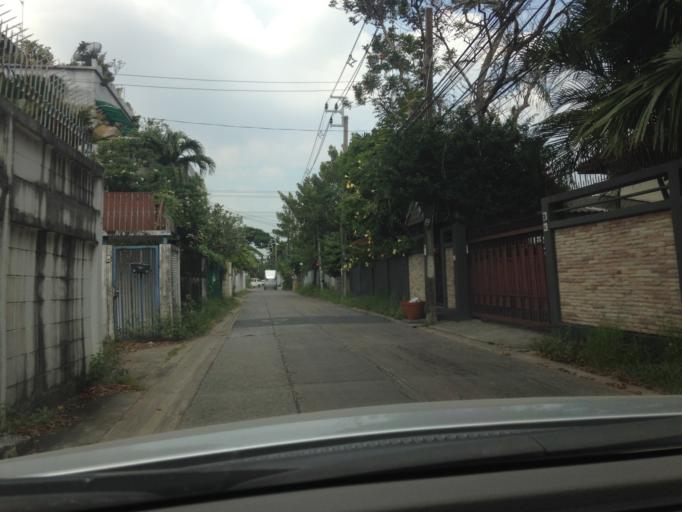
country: TH
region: Bangkok
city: Chatuchak
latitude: 13.8376
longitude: 100.5397
